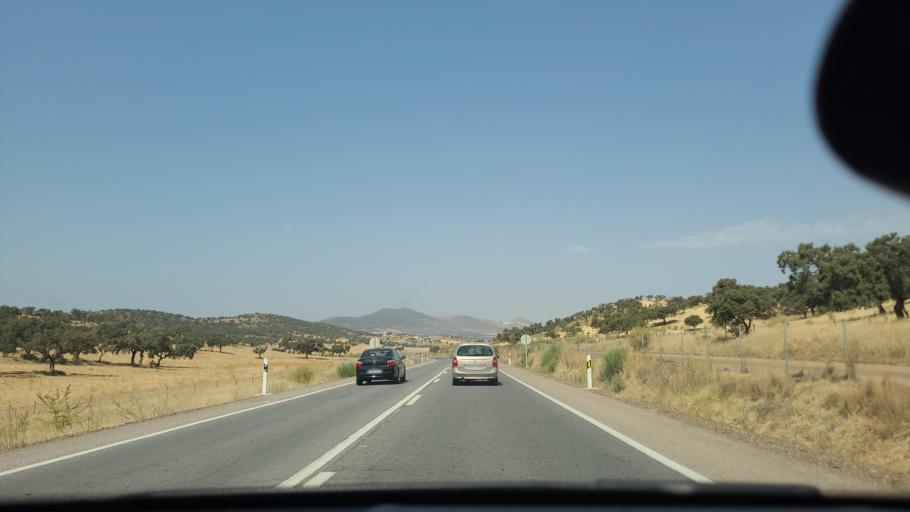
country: ES
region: Extremadura
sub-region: Provincia de Badajoz
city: Fuente del Maestre
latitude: 38.4728
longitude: -6.4529
